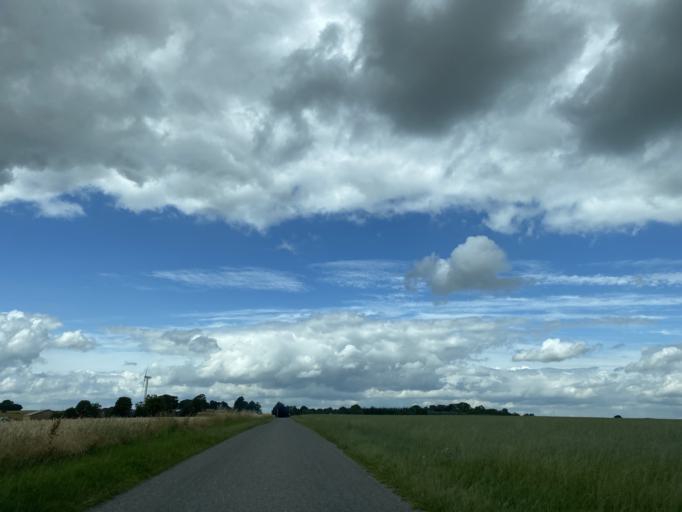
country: DK
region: Central Jutland
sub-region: Silkeborg Kommune
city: Svejbaek
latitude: 56.2377
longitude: 9.6433
